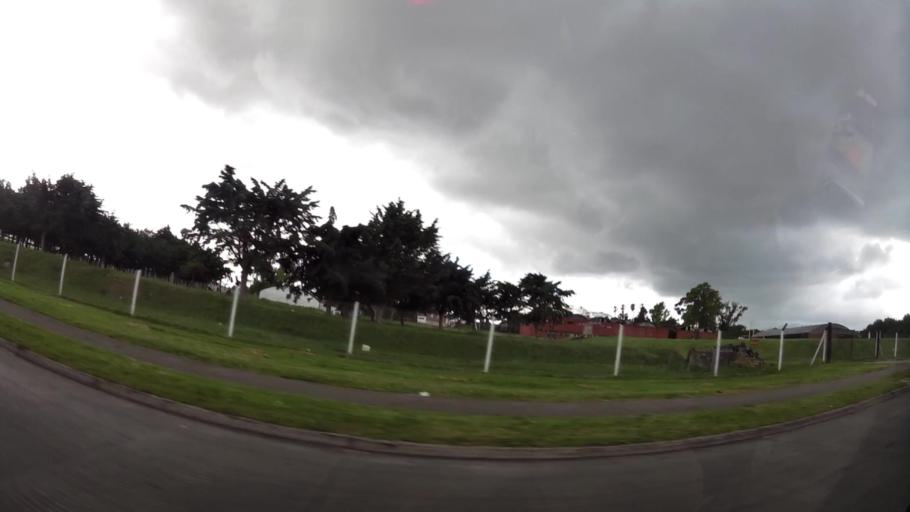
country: UY
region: Montevideo
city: Montevideo
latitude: -34.8469
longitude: -56.1699
